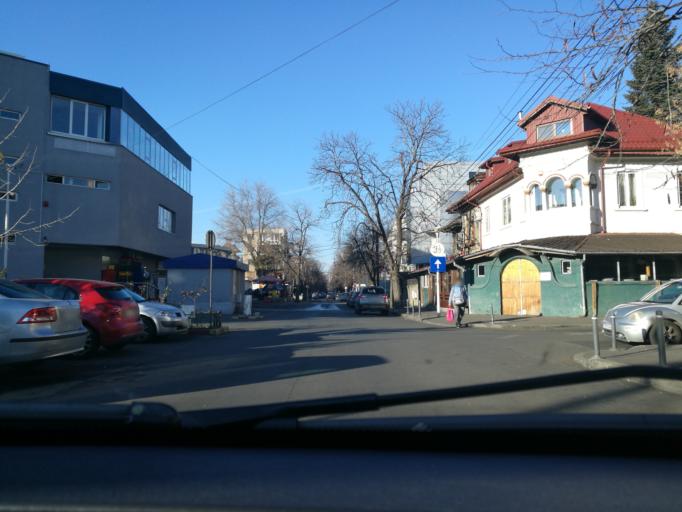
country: RO
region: Bucuresti
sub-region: Municipiul Bucuresti
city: Bucuresti
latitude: 44.4655
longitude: 26.0681
